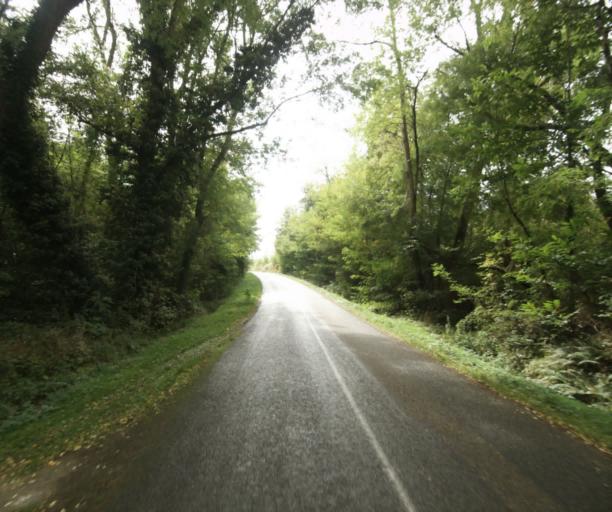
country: FR
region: Midi-Pyrenees
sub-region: Departement du Gers
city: Cazaubon
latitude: 43.8849
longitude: -0.0975
